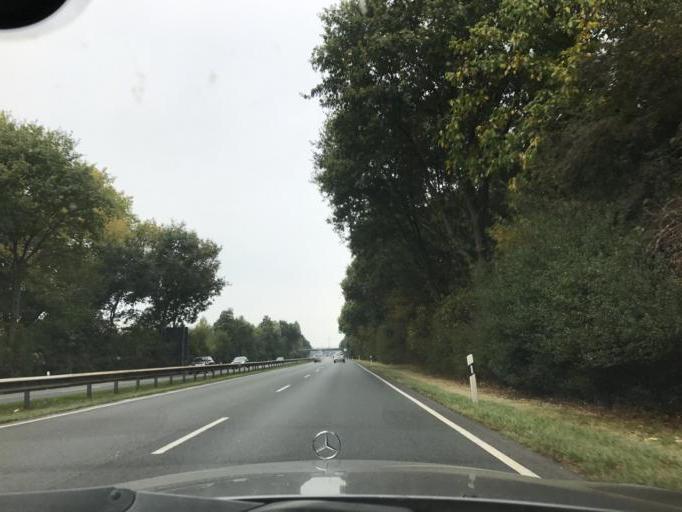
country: DE
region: Bremen
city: Bremen
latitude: 53.0450
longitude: 8.8307
